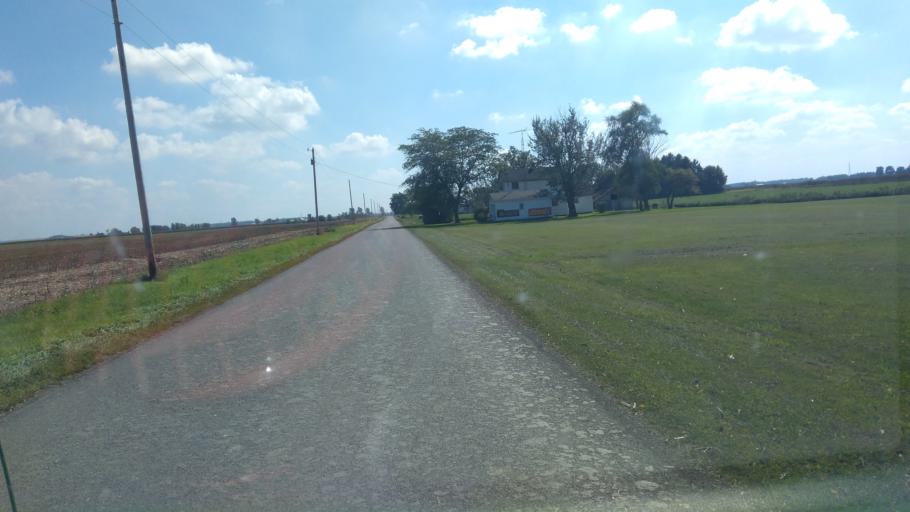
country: US
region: Ohio
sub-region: Hardin County
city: Ada
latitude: 40.6957
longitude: -83.8421
